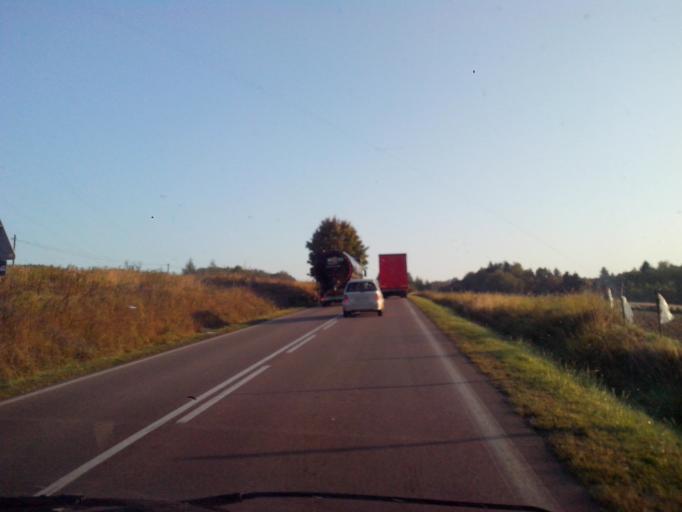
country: PL
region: Subcarpathian Voivodeship
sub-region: Powiat brzozowski
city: Wesola
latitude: 49.8168
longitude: 22.0511
